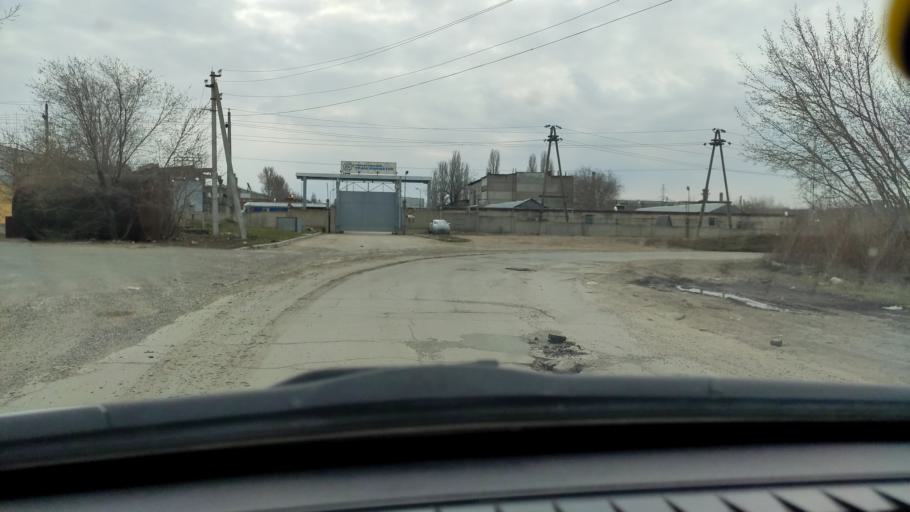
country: RU
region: Samara
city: Tol'yatti
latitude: 53.5270
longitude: 49.4604
